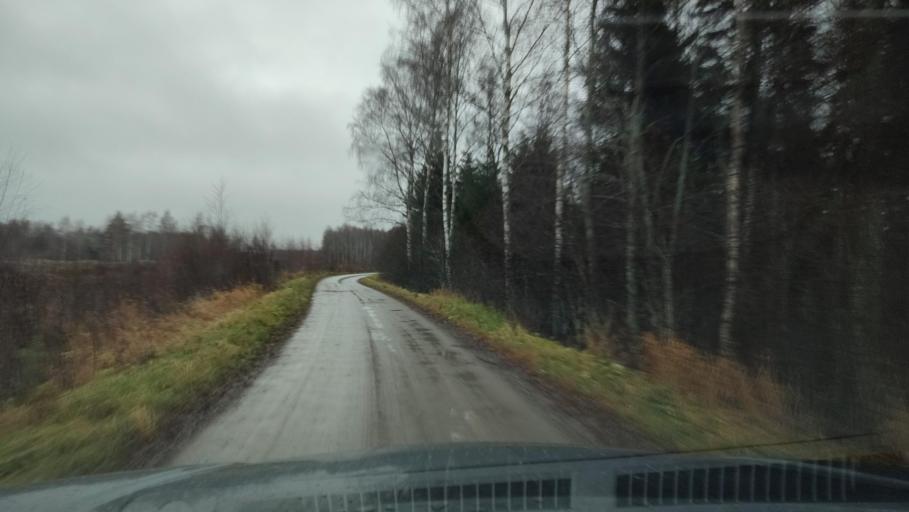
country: FI
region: Ostrobothnia
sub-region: Sydosterbotten
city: Kristinestad
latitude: 62.2380
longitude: 21.4664
